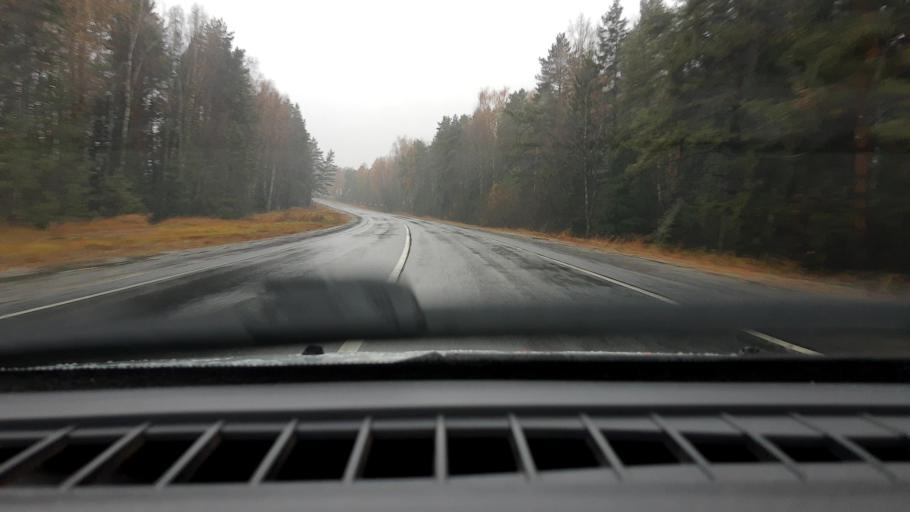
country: RU
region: Nizjnij Novgorod
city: Linda
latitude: 56.6785
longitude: 44.1486
